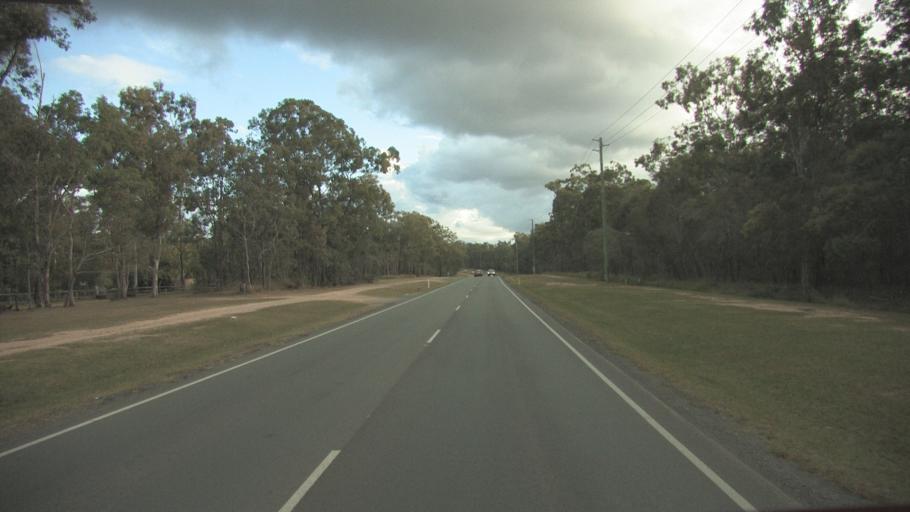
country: AU
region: Queensland
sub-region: Logan
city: Park Ridge South
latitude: -27.7106
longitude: 152.9977
